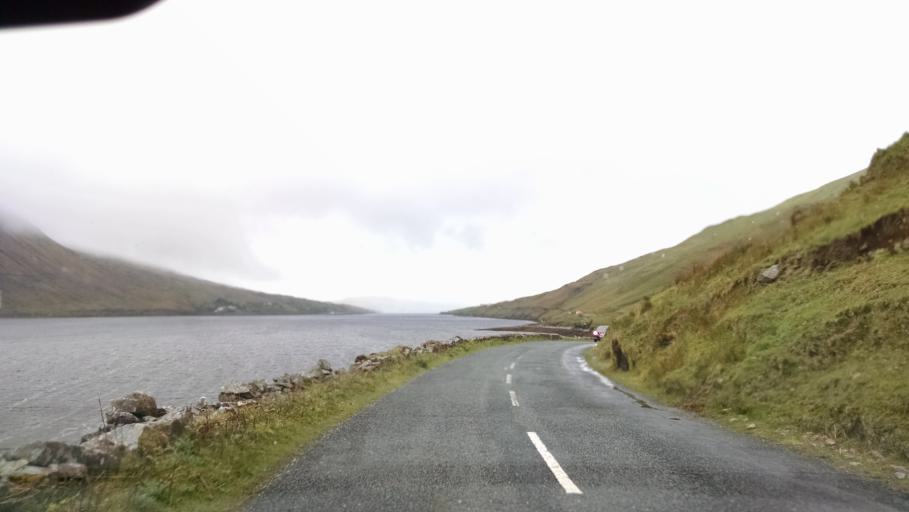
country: IE
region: Connaught
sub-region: Maigh Eo
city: Westport
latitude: 53.6045
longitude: -9.7005
